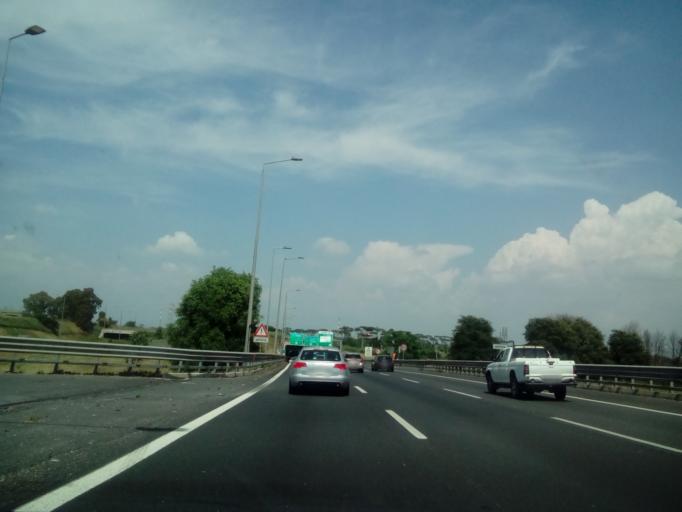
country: IT
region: Latium
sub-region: Citta metropolitana di Roma Capitale
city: Borgo Lotti
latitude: 41.8029
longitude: 12.5559
